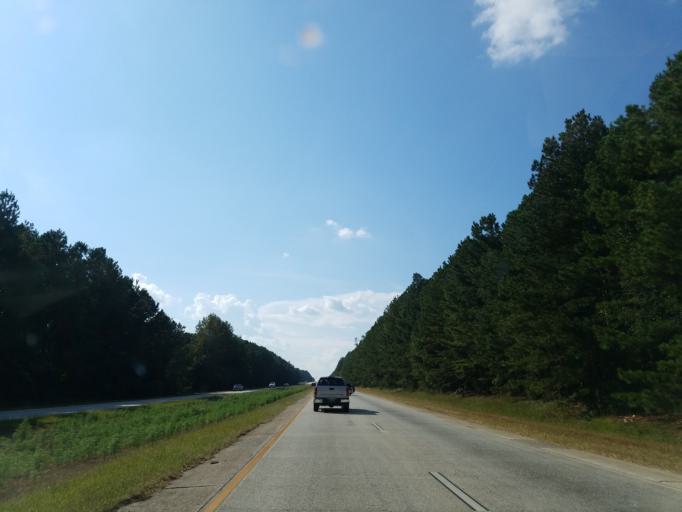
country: US
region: Georgia
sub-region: Barrow County
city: Auburn
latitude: 33.9592
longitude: -83.7873
